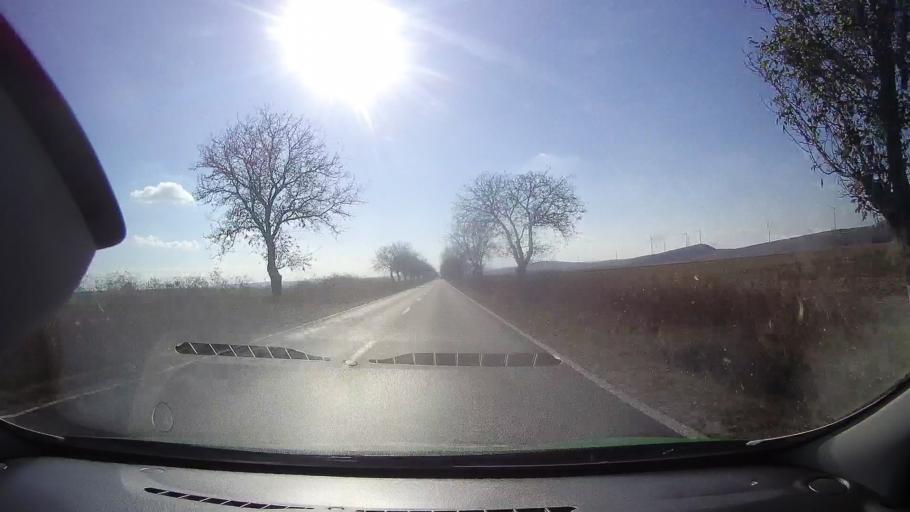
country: RO
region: Tulcea
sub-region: Comuna Ceamurlia de Jos
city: Ceamurlia de Jos
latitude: 44.7940
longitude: 28.6901
